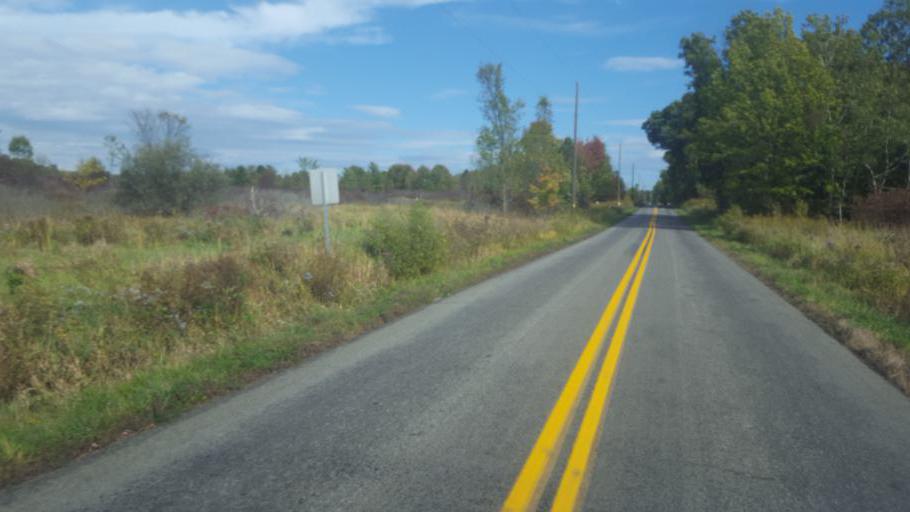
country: US
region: Pennsylvania
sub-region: Mercer County
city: Mercer
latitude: 41.3496
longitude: -80.2304
